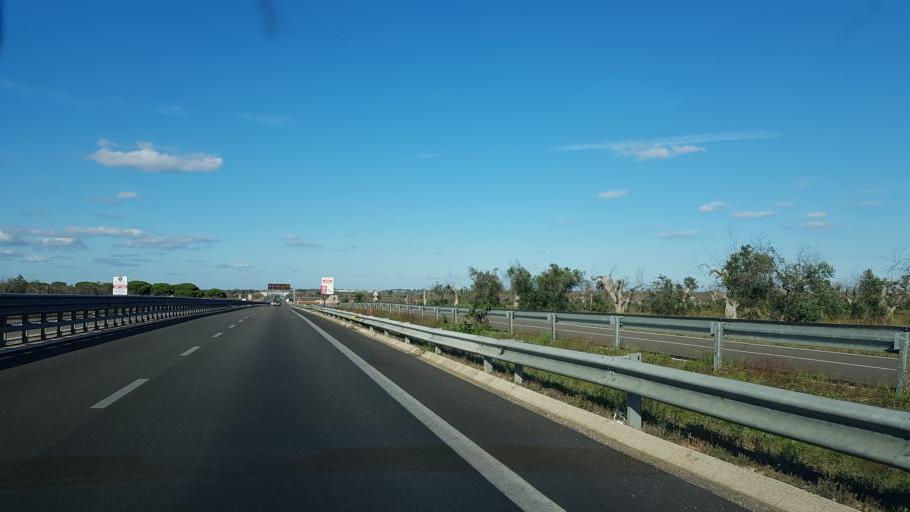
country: IT
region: Apulia
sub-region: Provincia di Lecce
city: Collemeto
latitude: 40.2458
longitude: 18.1136
